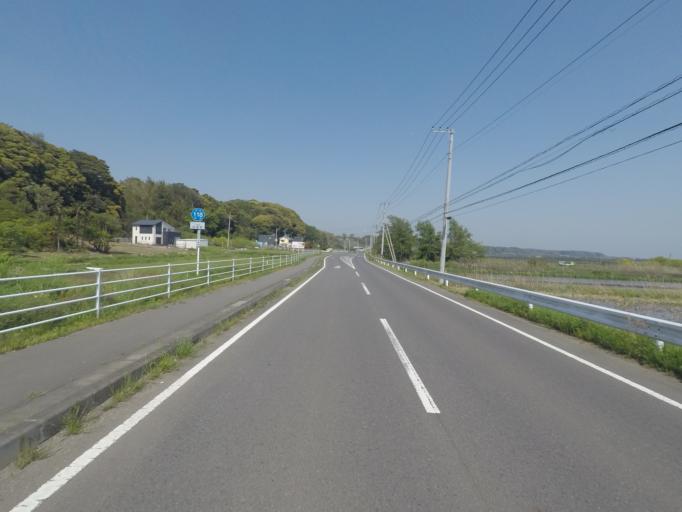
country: JP
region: Ibaraki
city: Ami
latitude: 36.0734
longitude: 140.2567
